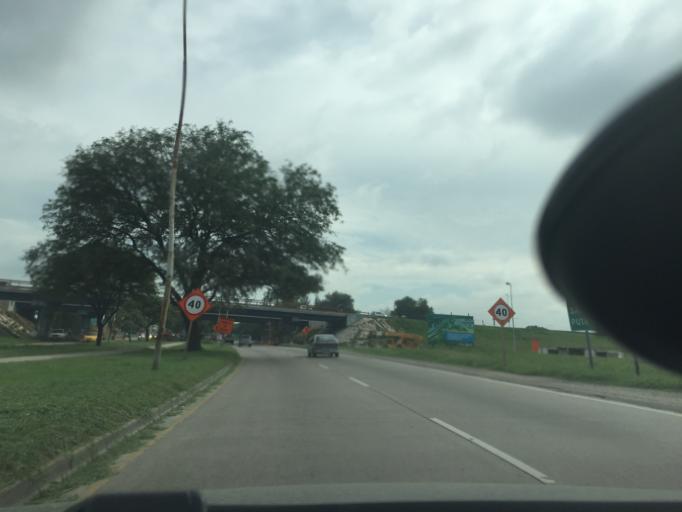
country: AR
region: Cordoba
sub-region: Departamento de Capital
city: Cordoba
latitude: -31.4628
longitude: -64.2202
